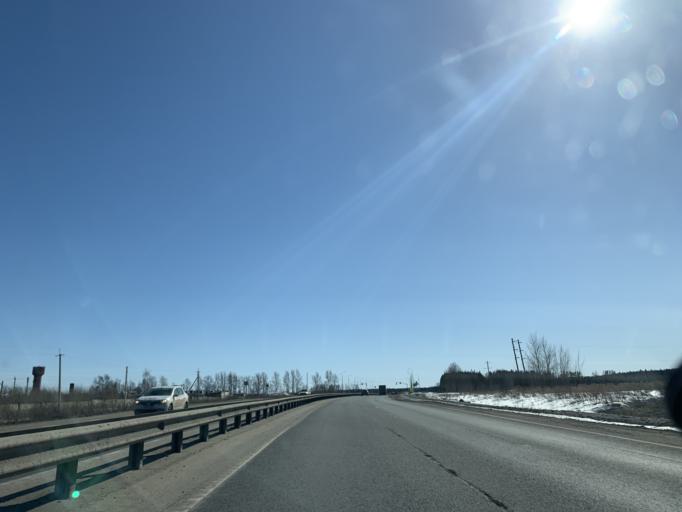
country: RU
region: Jaroslavl
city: Konstantinovskiy
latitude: 57.8391
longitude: 39.5536
